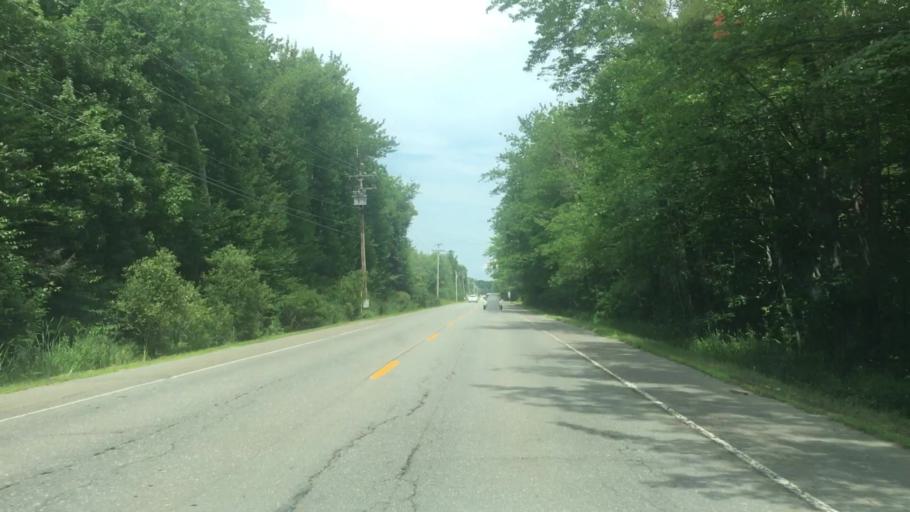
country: US
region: Maine
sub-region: Cumberland County
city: Scarborough
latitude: 43.5978
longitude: -70.2902
